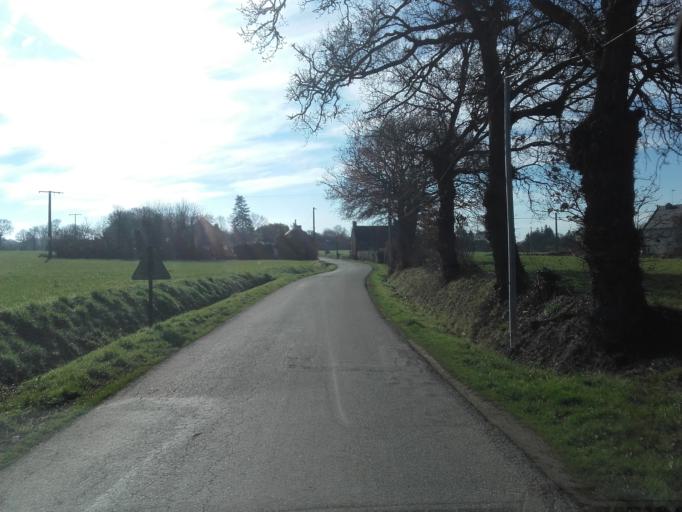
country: FR
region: Brittany
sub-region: Departement des Cotes-d'Armor
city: Pleguien
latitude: 48.6504
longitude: -2.9392
